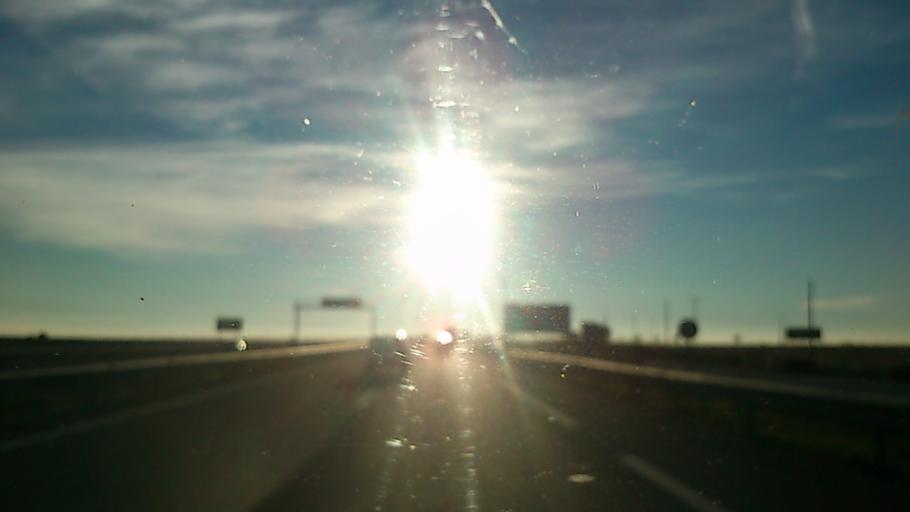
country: ES
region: Castille-La Mancha
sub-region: Provincia de Guadalajara
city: Muduex
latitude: 40.8122
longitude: -2.9374
